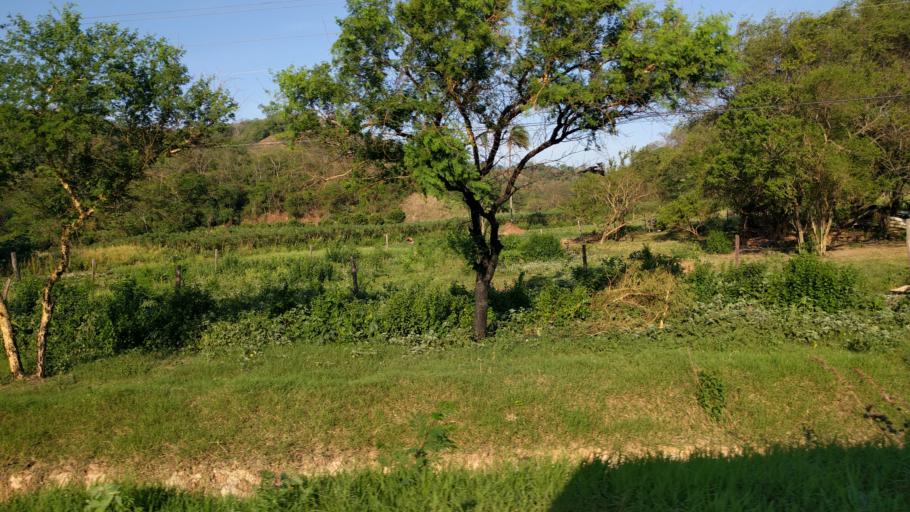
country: BO
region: Santa Cruz
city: Jorochito
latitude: -18.0918
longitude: -63.4505
